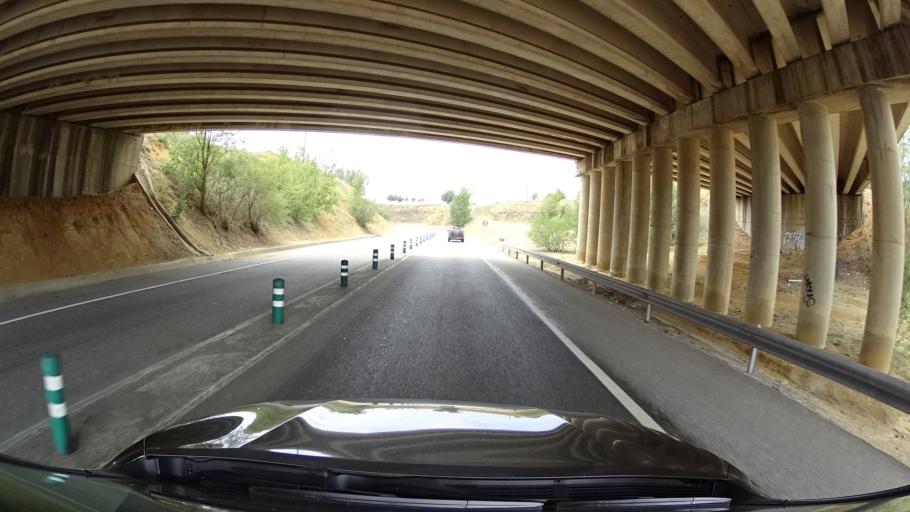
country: ES
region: Castille and Leon
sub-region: Provincia de Leon
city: Leon
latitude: 42.6196
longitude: -5.5829
